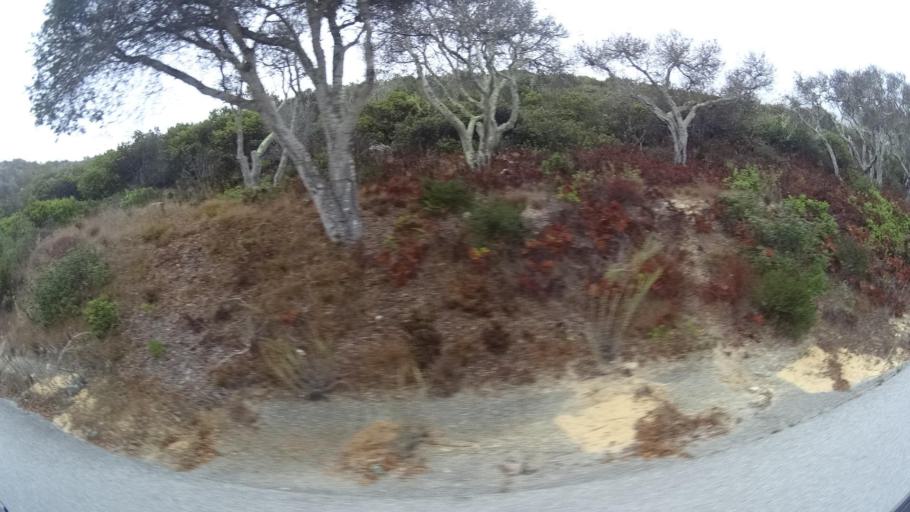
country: US
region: California
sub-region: Monterey County
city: Marina
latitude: 36.6284
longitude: -121.7399
